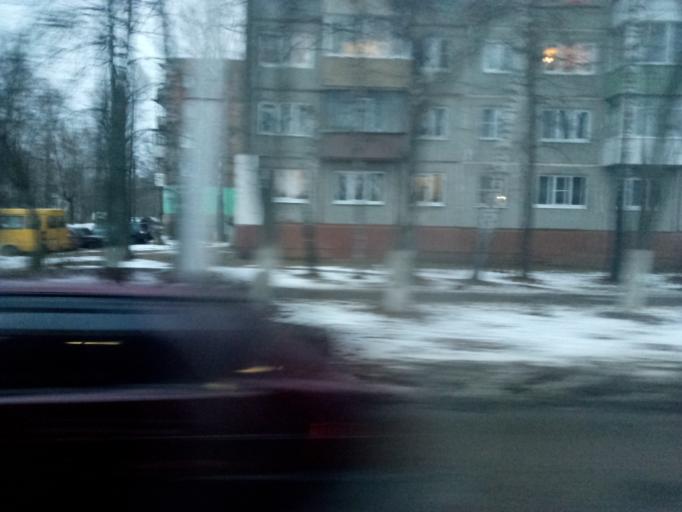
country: RU
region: Tula
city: Kosaya Gora
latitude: 54.1933
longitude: 37.5352
